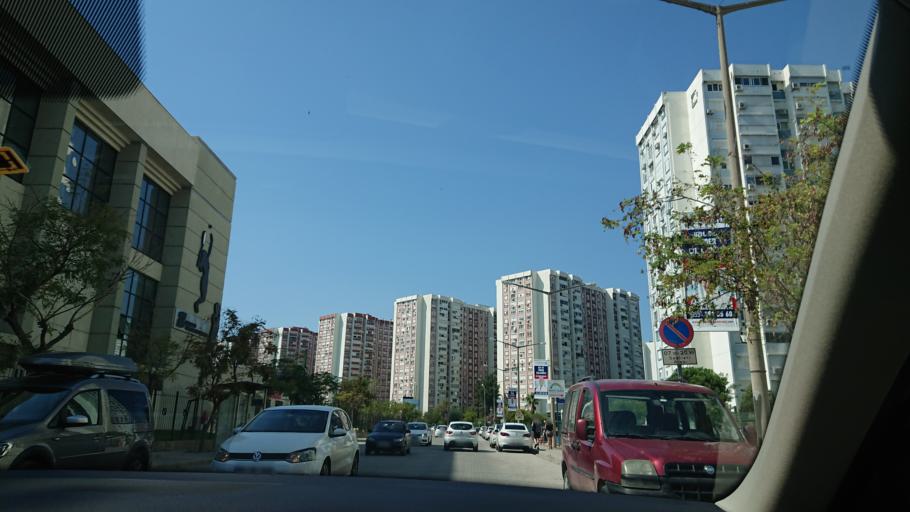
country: TR
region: Izmir
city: Karsiyaka
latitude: 38.4684
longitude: 27.0810
